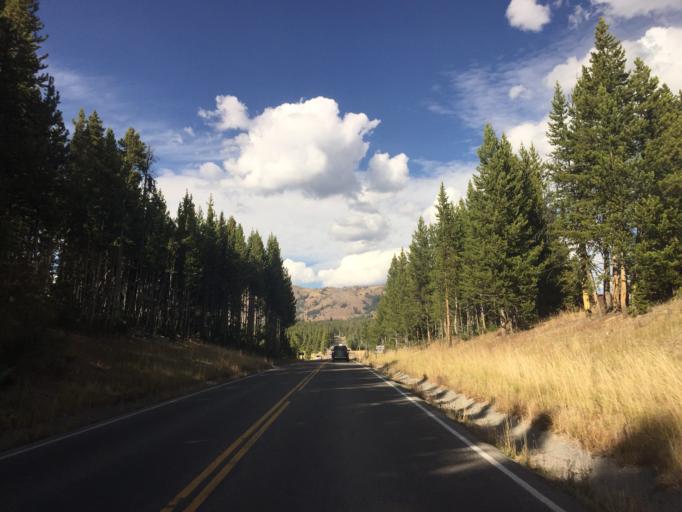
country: US
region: Montana
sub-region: Gallatin County
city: West Yellowstone
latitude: 44.7309
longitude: -110.4936
